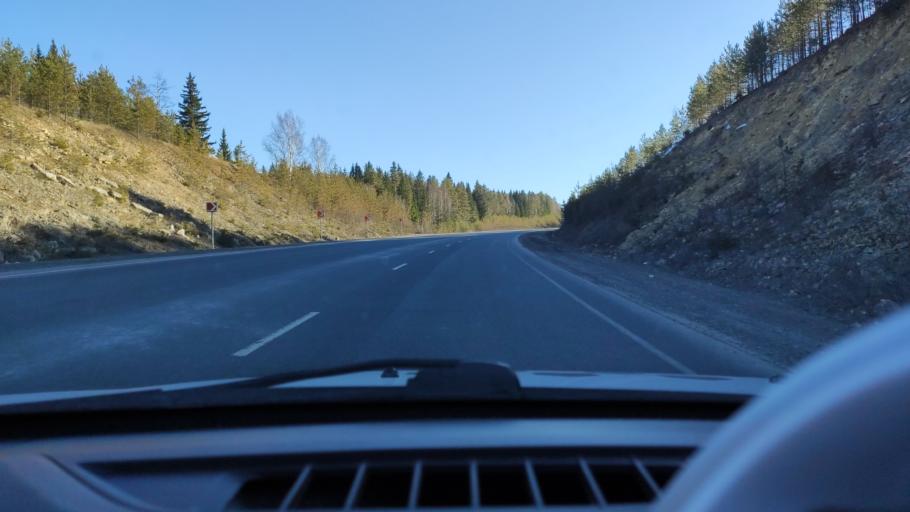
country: RU
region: Perm
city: Suksun
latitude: 57.1203
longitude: 57.3086
